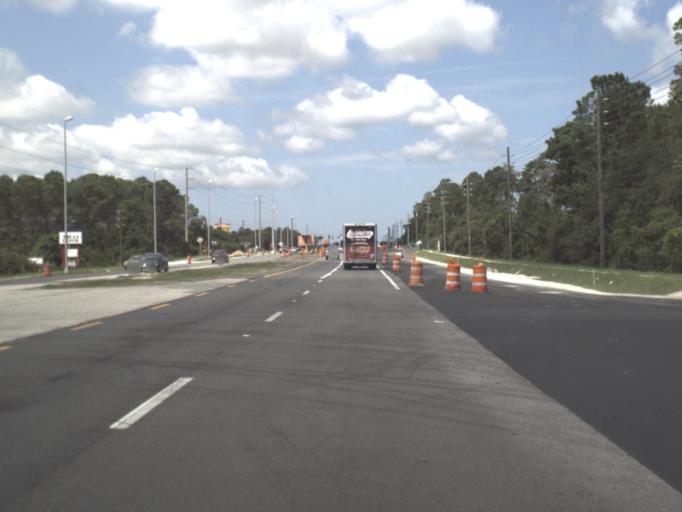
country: US
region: Florida
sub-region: Hernando County
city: North Weeki Wachee
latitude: 28.5232
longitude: -82.5604
